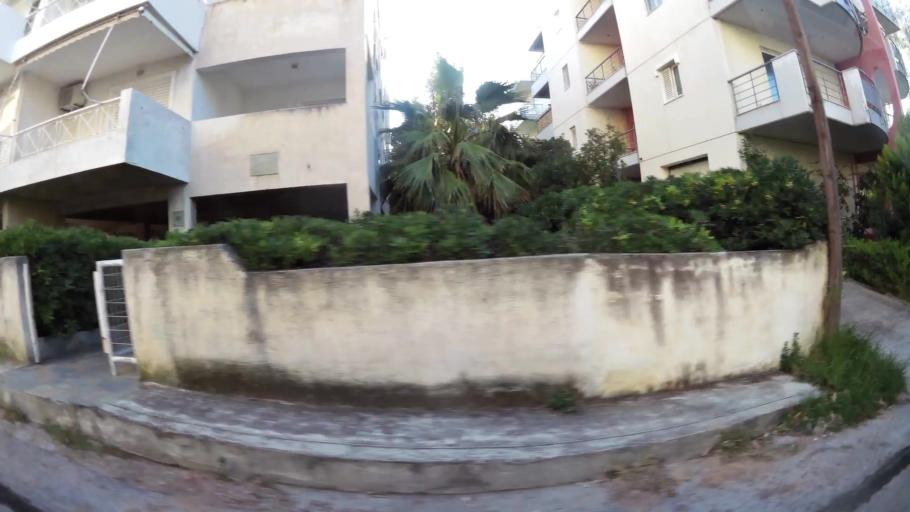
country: GR
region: Attica
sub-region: Nomarchia Anatolikis Attikis
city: Rafina
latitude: 38.0155
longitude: 24.0150
